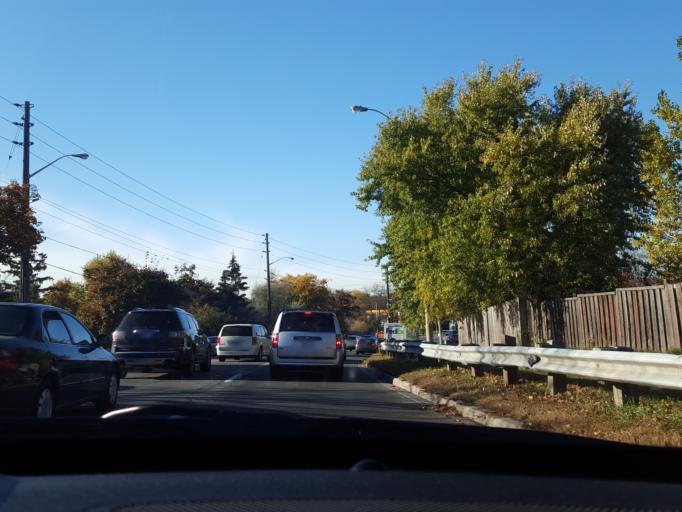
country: CA
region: Ontario
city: Scarborough
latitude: 43.8046
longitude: -79.2763
